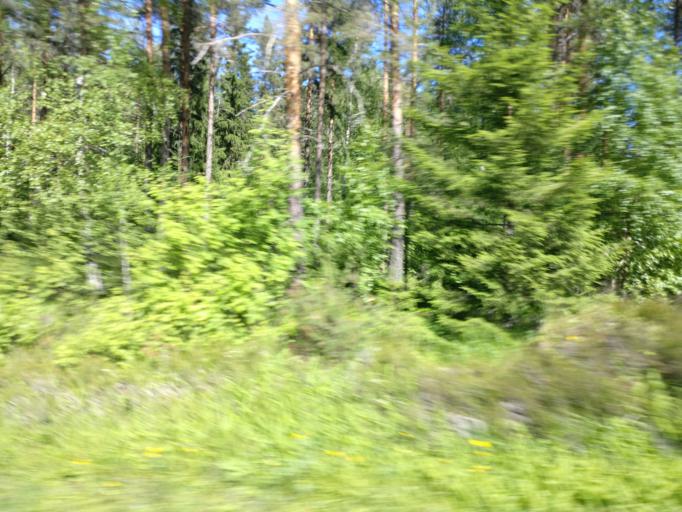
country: FI
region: Southern Savonia
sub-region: Savonlinna
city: Rantasalmi
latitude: 62.0925
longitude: 28.2807
